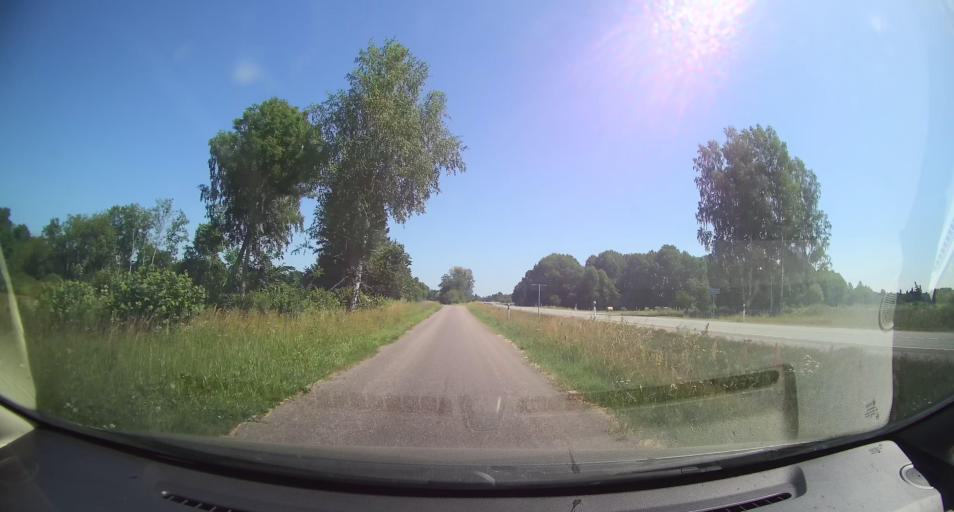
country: EE
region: Laeaene
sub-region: Lihula vald
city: Lihula
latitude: 58.6252
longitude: 23.6527
